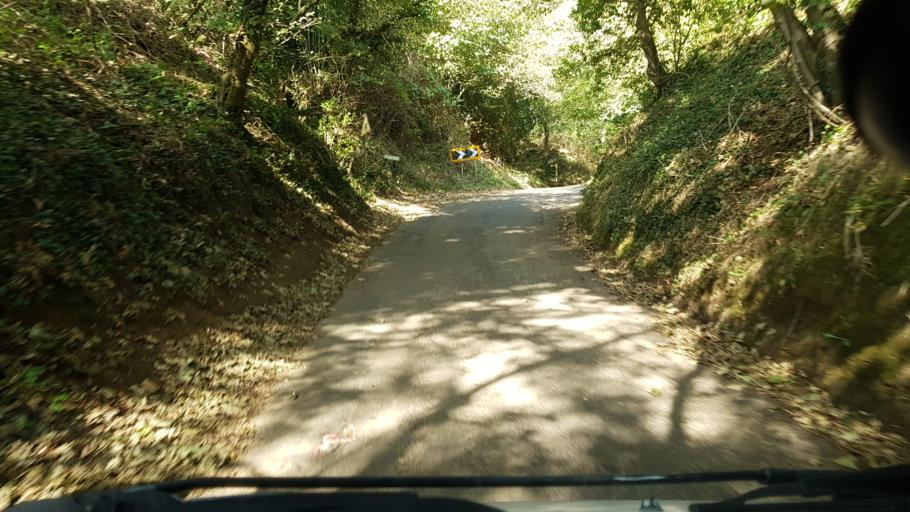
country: GB
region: England
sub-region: Surrey
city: Guildford
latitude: 51.2217
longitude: -0.5973
